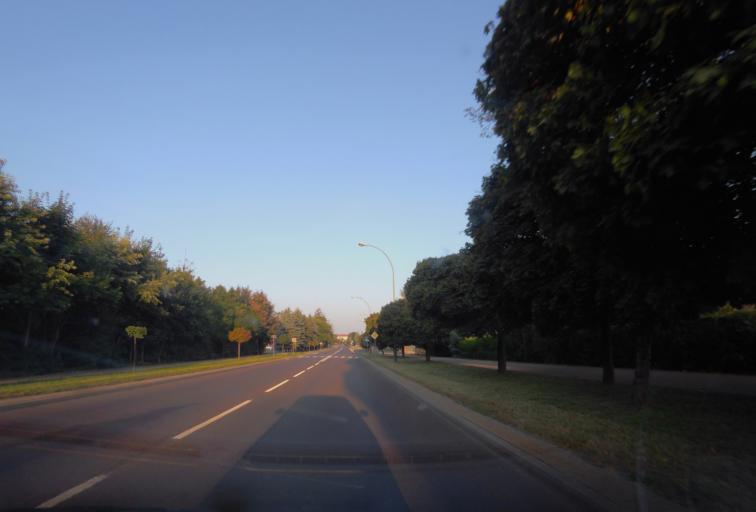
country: PL
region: Lublin Voivodeship
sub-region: Powiat janowski
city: Janow Lubelski
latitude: 50.7009
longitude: 22.4287
